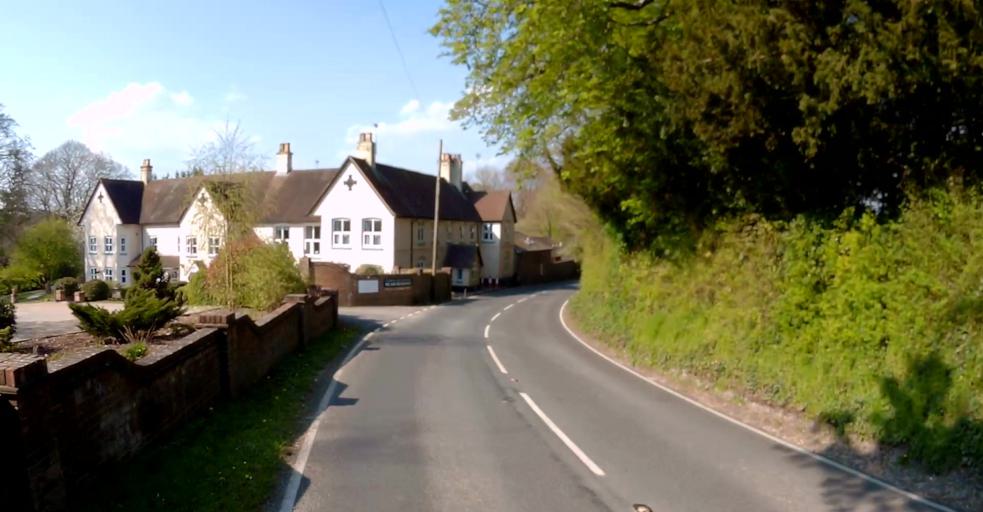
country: GB
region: England
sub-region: Hampshire
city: Four Marks
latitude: 51.1000
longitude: -1.1620
